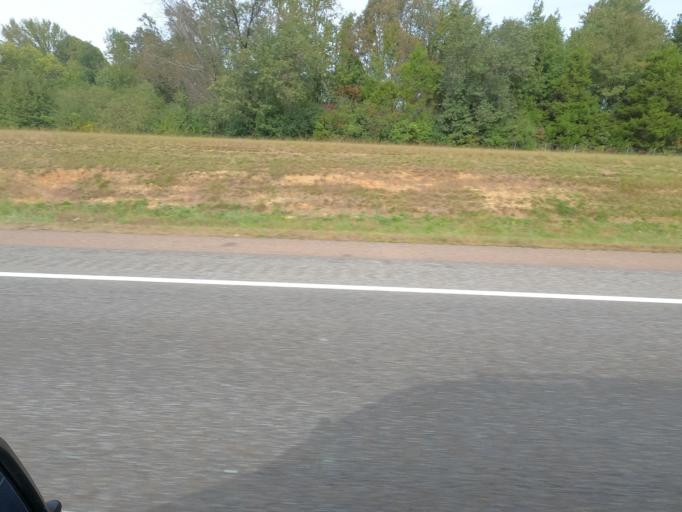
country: US
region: Tennessee
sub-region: Henderson County
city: Lexington
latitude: 35.7697
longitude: -88.4523
